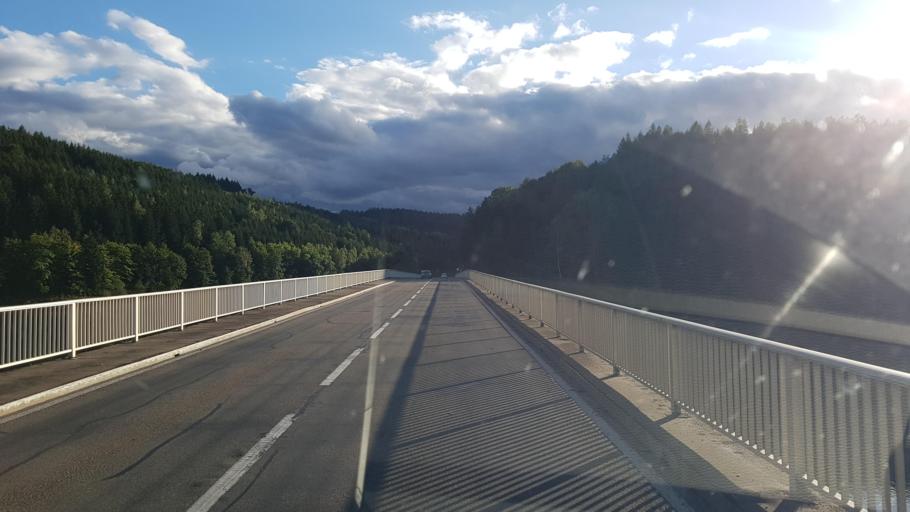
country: DE
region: Thuringia
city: Harra
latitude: 50.4507
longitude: 11.6929
